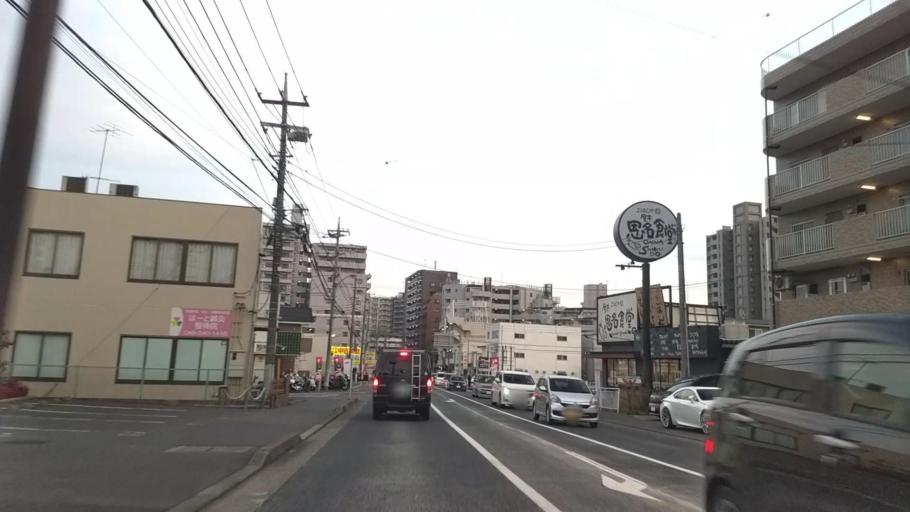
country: JP
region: Kanagawa
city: Atsugi
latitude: 35.4443
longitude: 139.3544
